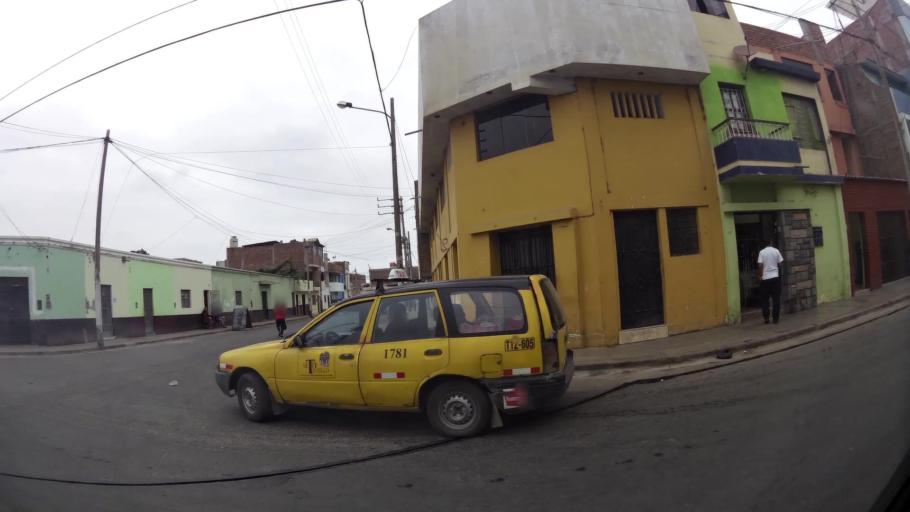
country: PE
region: La Libertad
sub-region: Provincia de Trujillo
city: Trujillo
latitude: -8.1147
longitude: -79.0199
